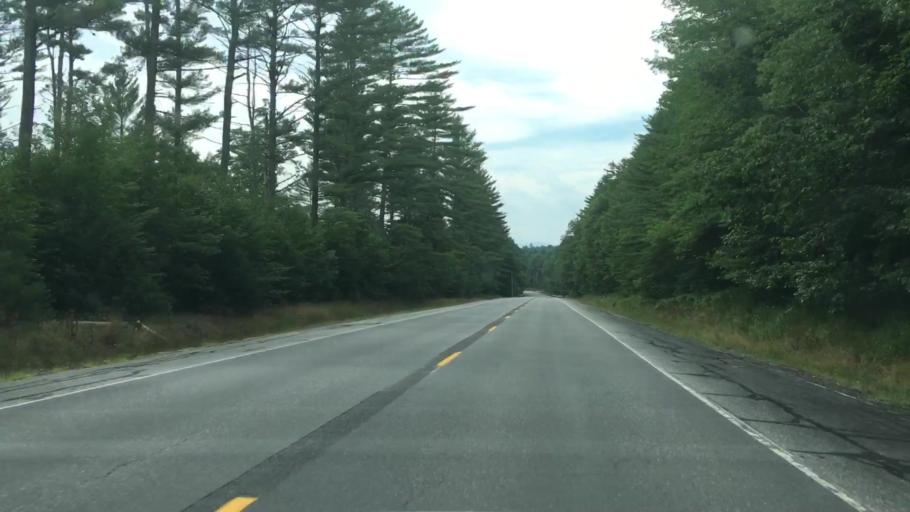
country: US
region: Maine
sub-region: Oxford County
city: Bethel
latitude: 44.4861
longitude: -70.7436
